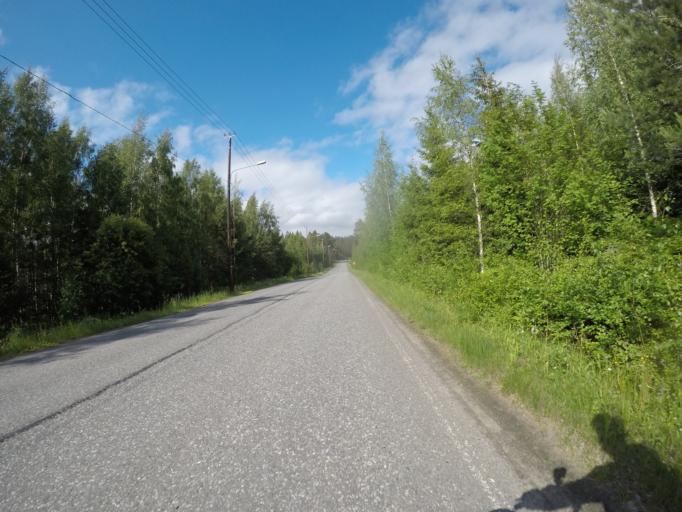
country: FI
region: Haeme
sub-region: Haemeenlinna
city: Haemeenlinna
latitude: 60.9687
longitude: 24.4245
